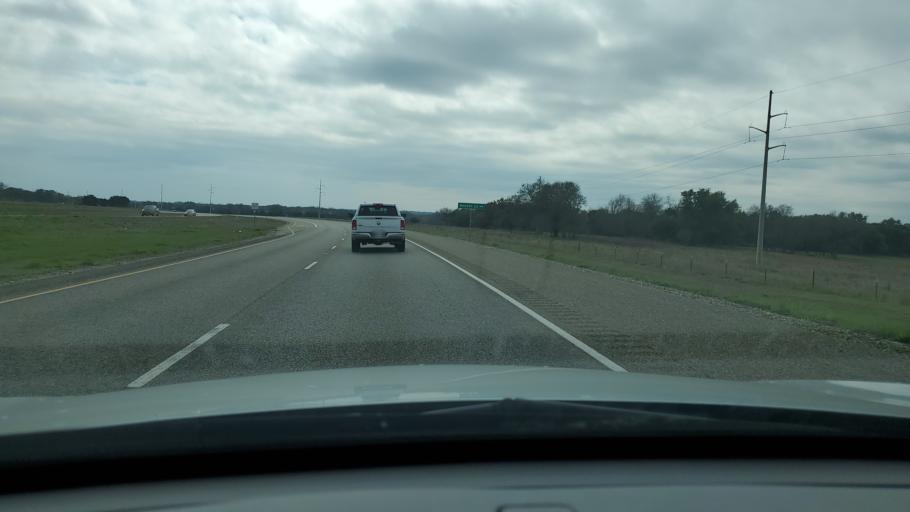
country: US
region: Texas
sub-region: Williamson County
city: Florence
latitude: 30.7736
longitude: -97.7590
